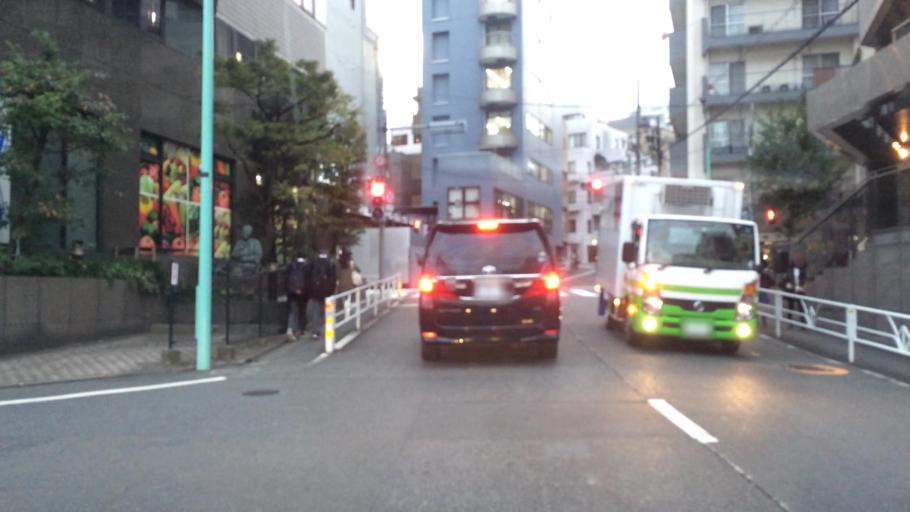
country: JP
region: Tokyo
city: Tokyo
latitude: 35.6508
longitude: 139.7077
